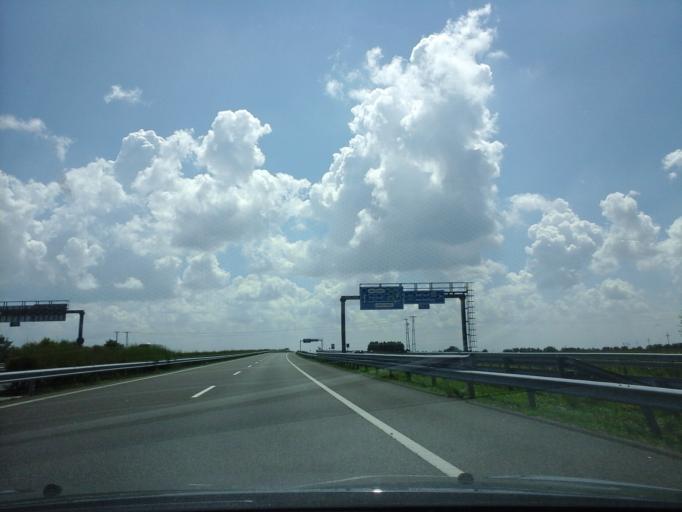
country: HU
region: Hajdu-Bihar
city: Debrecen
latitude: 47.5568
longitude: 21.5503
